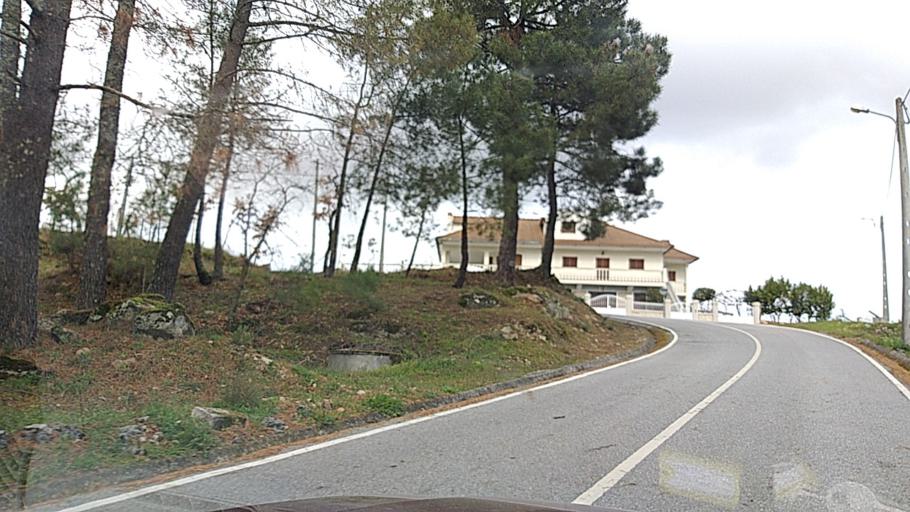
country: PT
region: Viseu
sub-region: Satao
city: Satao
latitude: 40.6578
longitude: -7.6572
